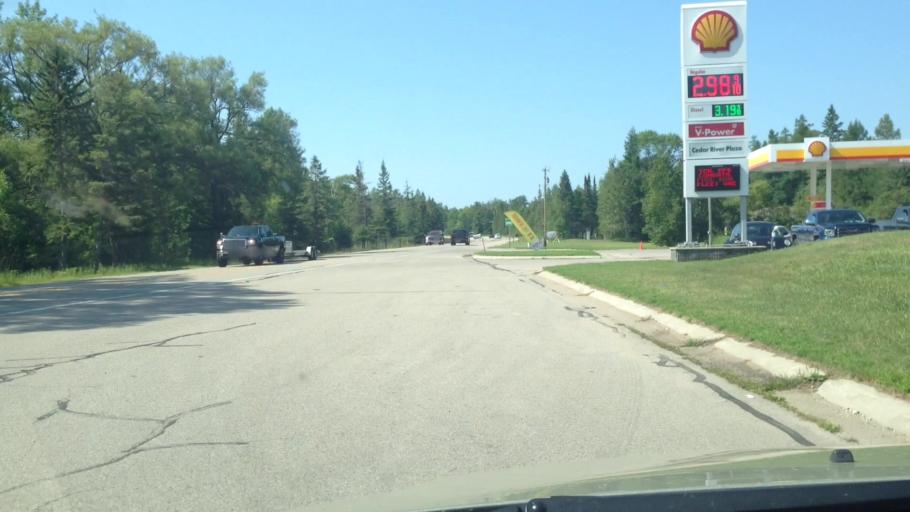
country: US
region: Michigan
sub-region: Menominee County
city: Menominee
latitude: 45.4099
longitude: -87.3567
